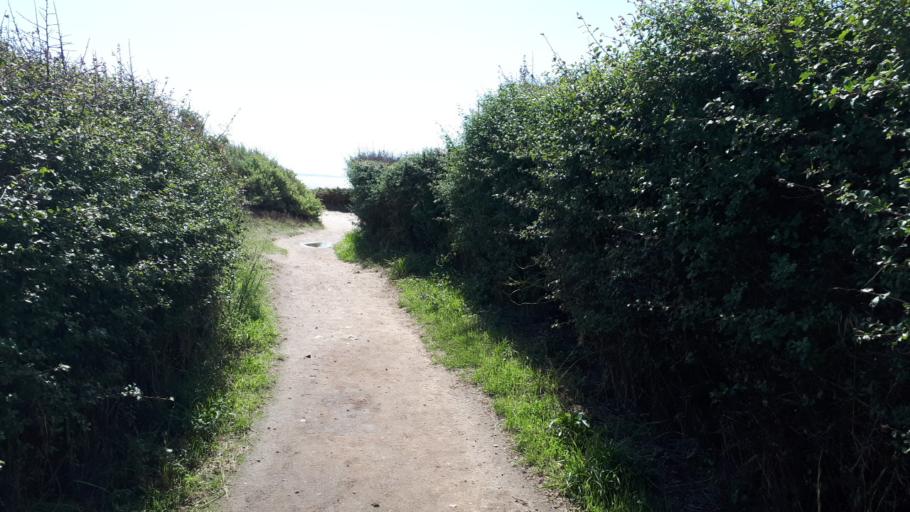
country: FR
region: Brittany
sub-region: Departement du Morbihan
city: Penestin
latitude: 47.4887
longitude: -2.5012
